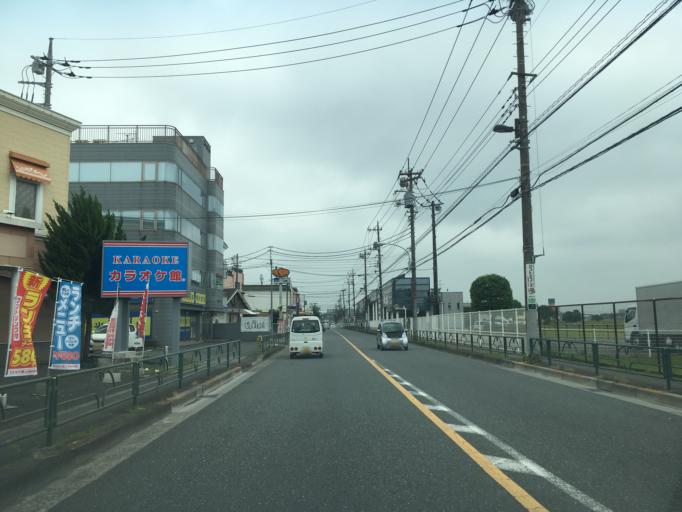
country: JP
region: Tokyo
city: Hino
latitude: 35.7402
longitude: 139.3939
